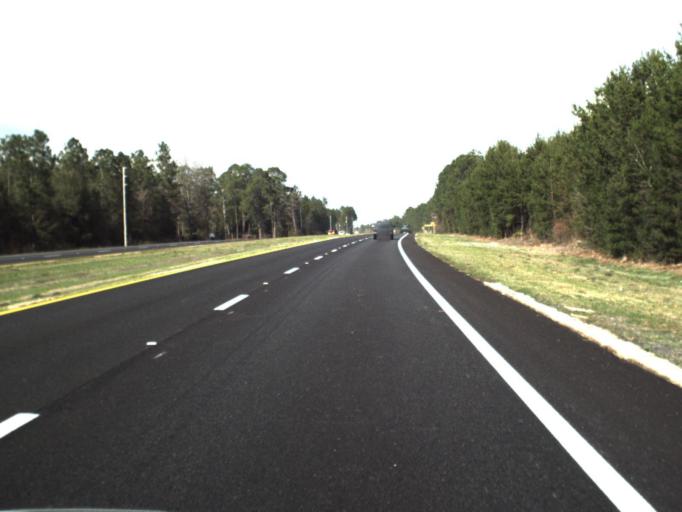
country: US
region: Florida
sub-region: Bay County
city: Youngstown
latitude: 30.4011
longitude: -85.4342
